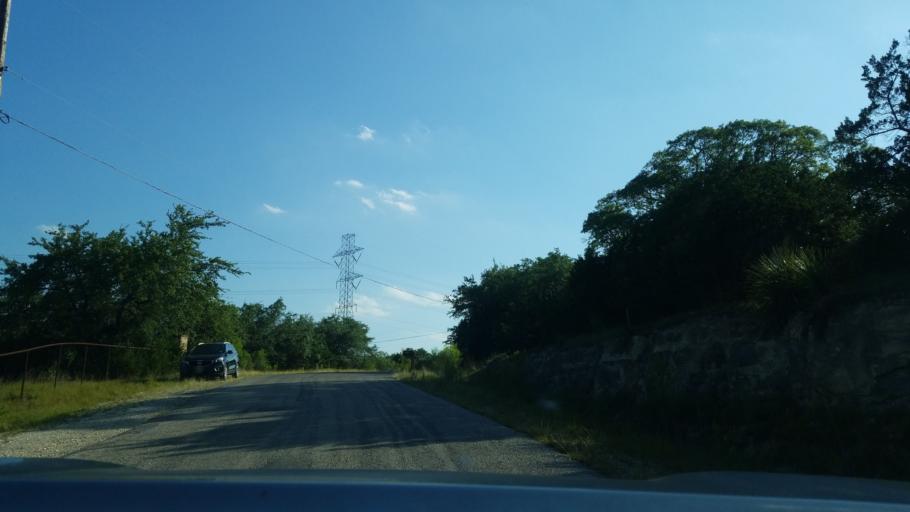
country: US
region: Texas
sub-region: Comal County
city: Bulverde
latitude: 29.7802
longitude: -98.4301
